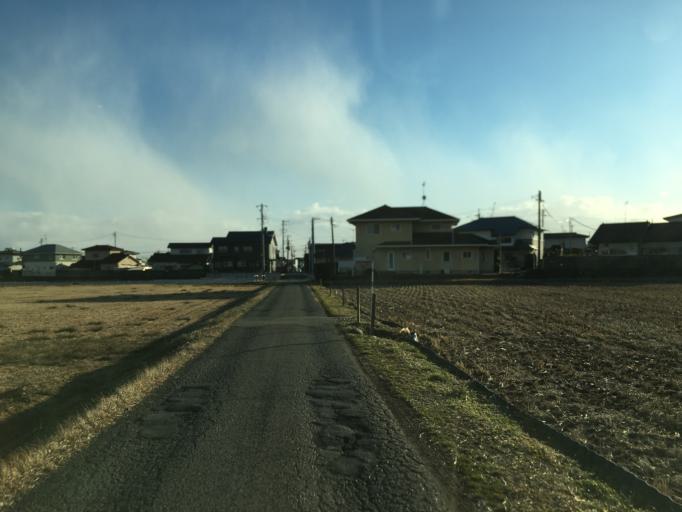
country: JP
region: Fukushima
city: Fukushima-shi
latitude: 37.7719
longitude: 140.4301
